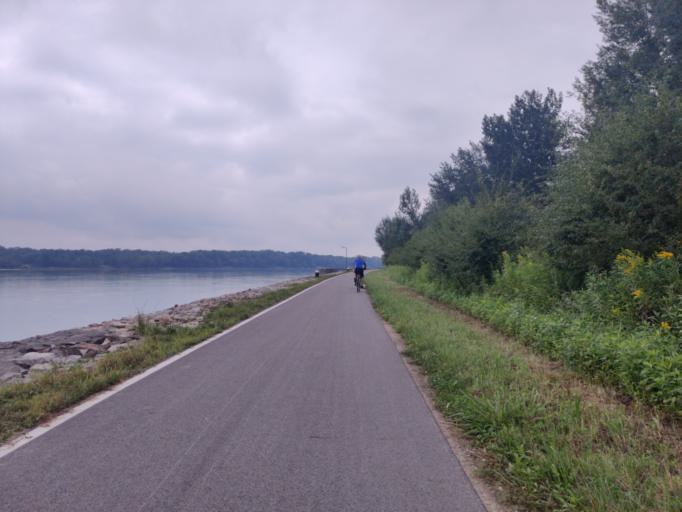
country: AT
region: Lower Austria
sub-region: Politischer Bezirk Tulln
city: Kirchberg am Wagram
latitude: 48.3709
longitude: 15.8685
